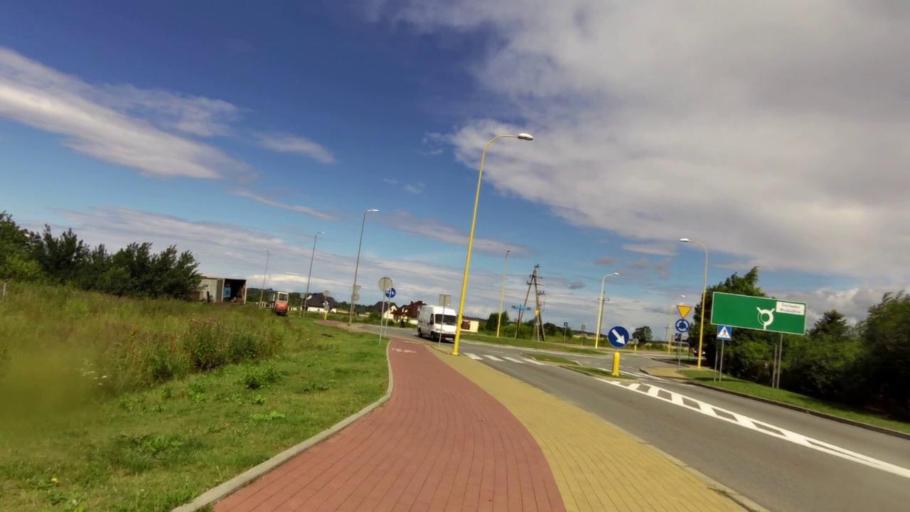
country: PL
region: West Pomeranian Voivodeship
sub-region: Powiat slawienski
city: Darlowo
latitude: 54.4276
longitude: 16.4153
